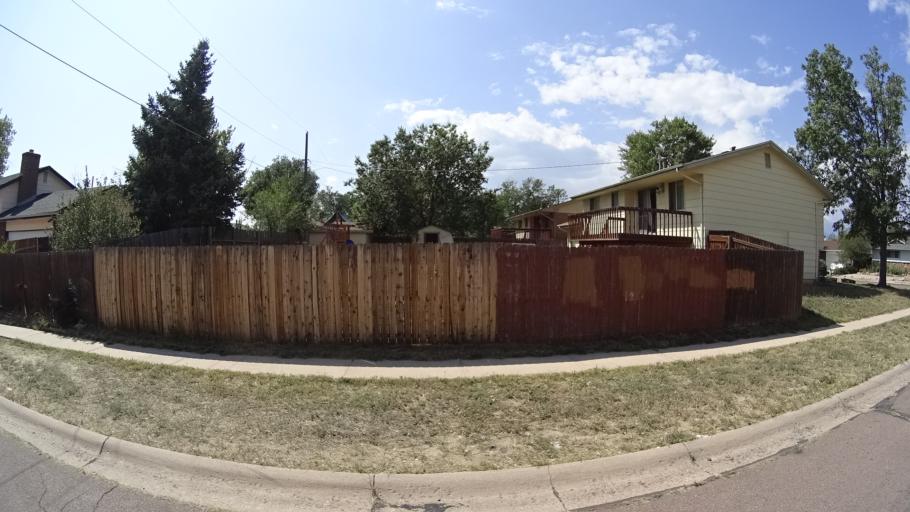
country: US
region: Colorado
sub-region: El Paso County
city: Colorado Springs
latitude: 38.8289
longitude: -104.7649
